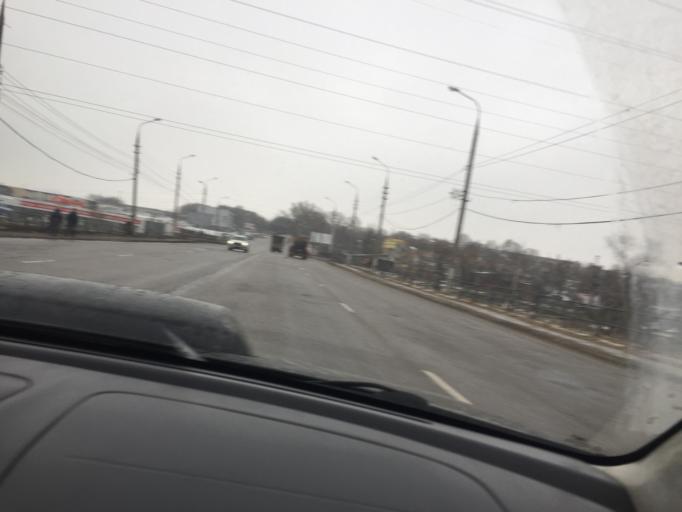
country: RU
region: Tula
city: Tula
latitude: 54.1726
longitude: 37.6359
